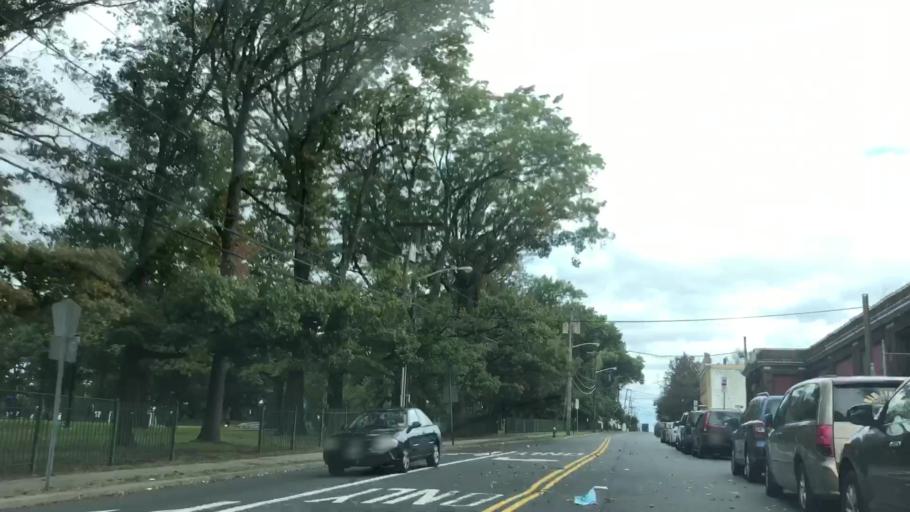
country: US
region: New Jersey
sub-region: Essex County
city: Irvington
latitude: 40.7179
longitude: -74.2272
